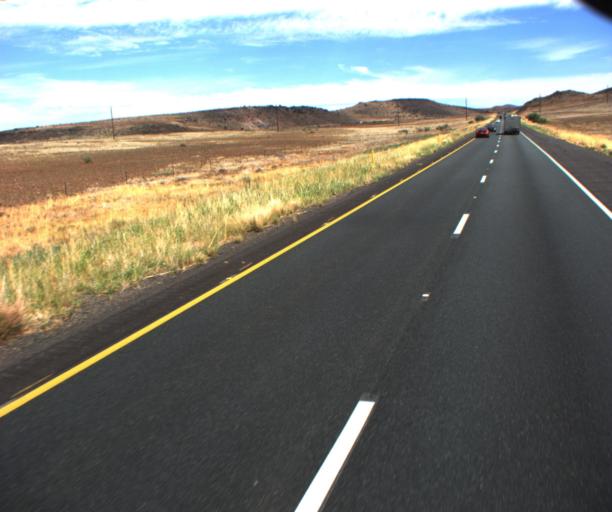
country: US
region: Arizona
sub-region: Yavapai County
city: Cordes Lakes
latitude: 34.4385
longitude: -112.0311
